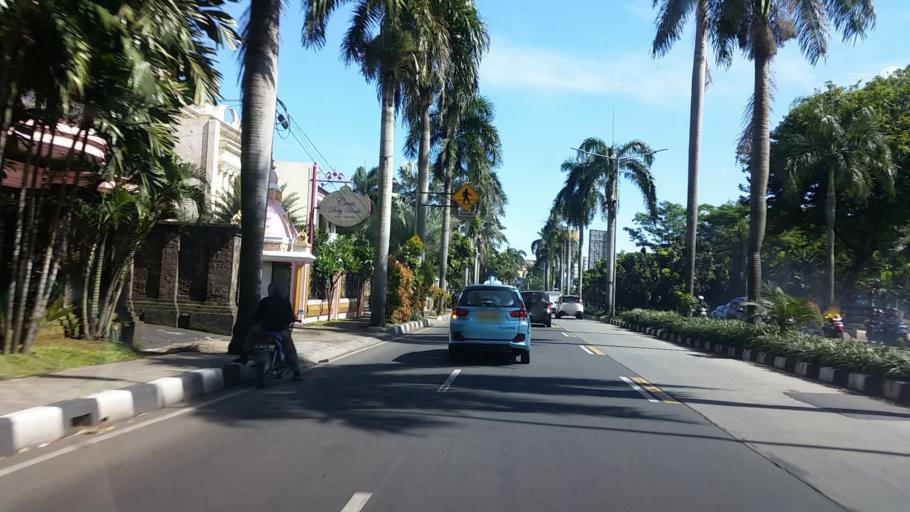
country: ID
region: Banten
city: South Tangerang
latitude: -6.2726
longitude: 106.7828
